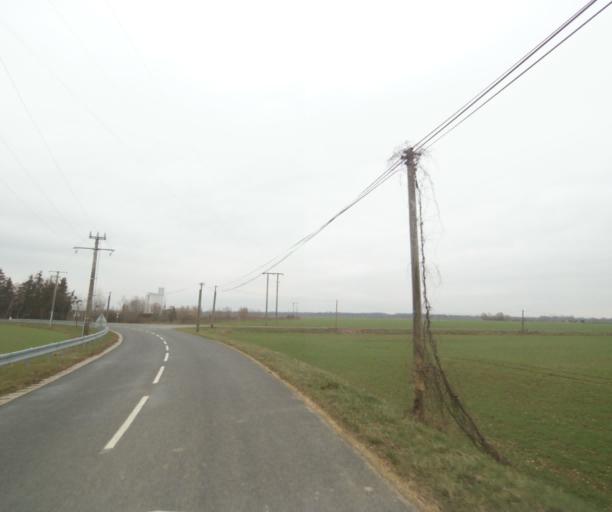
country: FR
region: Champagne-Ardenne
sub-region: Departement de la Haute-Marne
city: Villiers-en-Lieu
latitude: 48.6443
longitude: 4.7677
